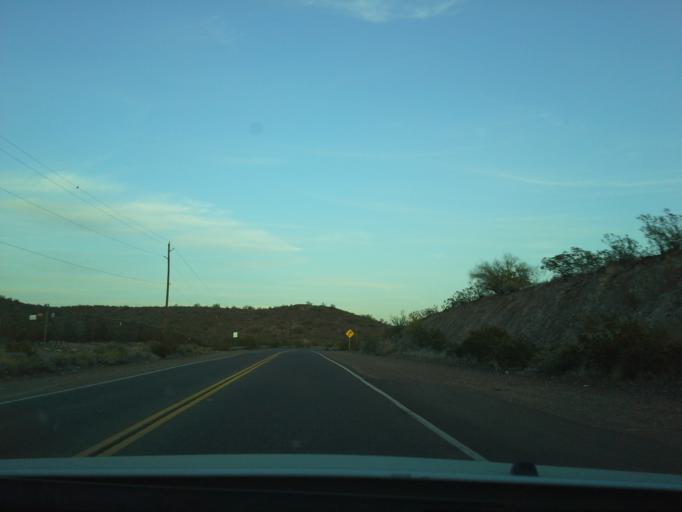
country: US
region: Arizona
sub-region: Maricopa County
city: Cave Creek
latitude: 33.7129
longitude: -112.0719
